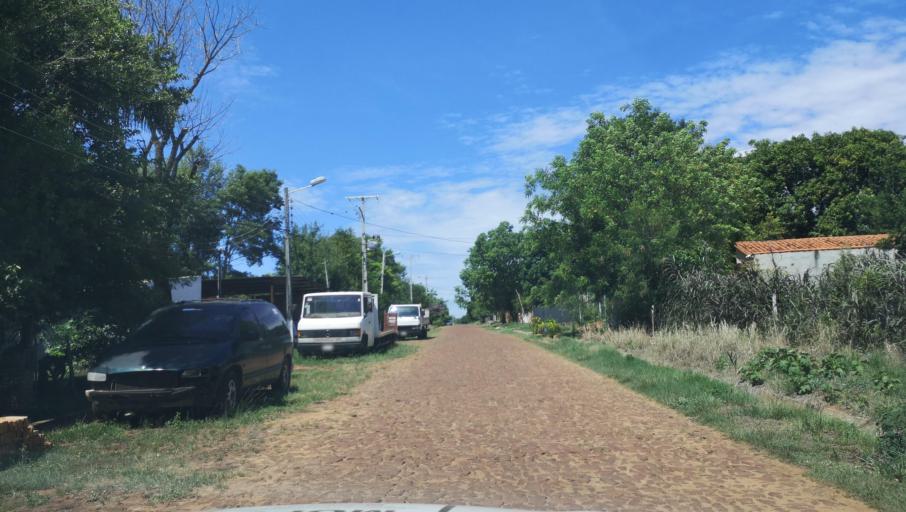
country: PY
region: Misiones
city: Santa Maria
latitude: -26.8746
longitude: -57.0305
